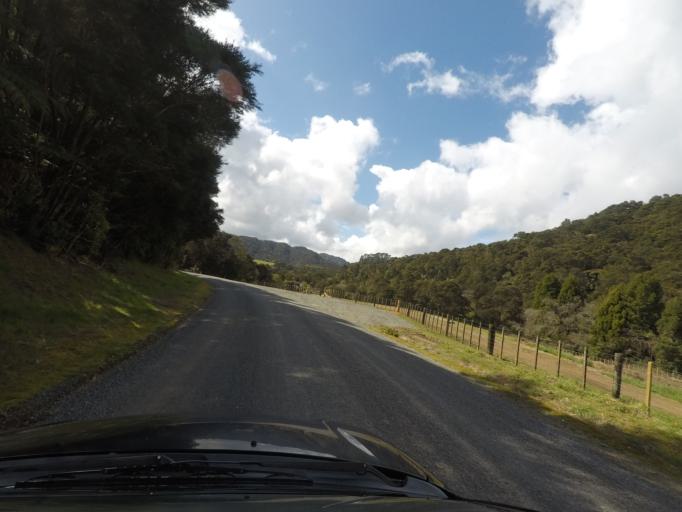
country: NZ
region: Auckland
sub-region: Auckland
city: Red Hill
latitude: -37.0930
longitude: 175.1535
